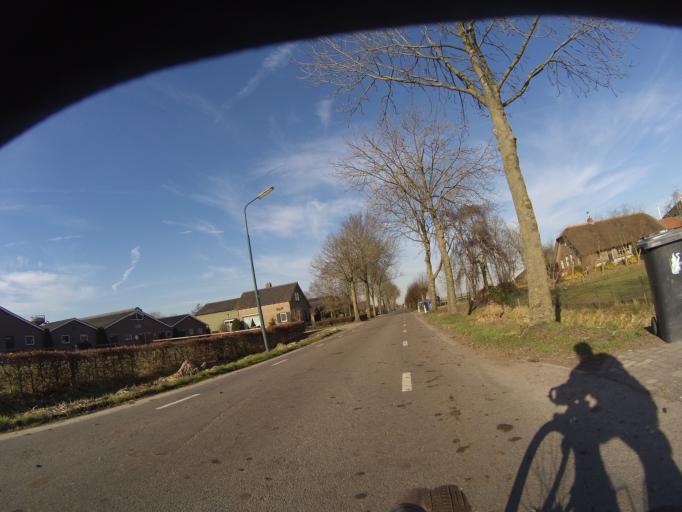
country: NL
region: Utrecht
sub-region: Gemeente Bunschoten
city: Bunschoten
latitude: 52.2137
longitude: 5.3892
